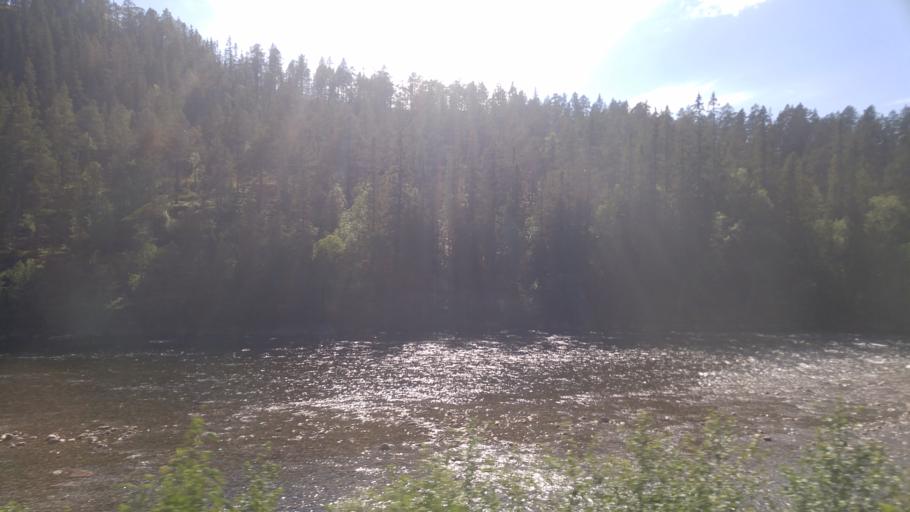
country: NO
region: Sor-Trondelag
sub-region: Selbu
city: Mebonden
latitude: 62.9683
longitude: 10.9538
